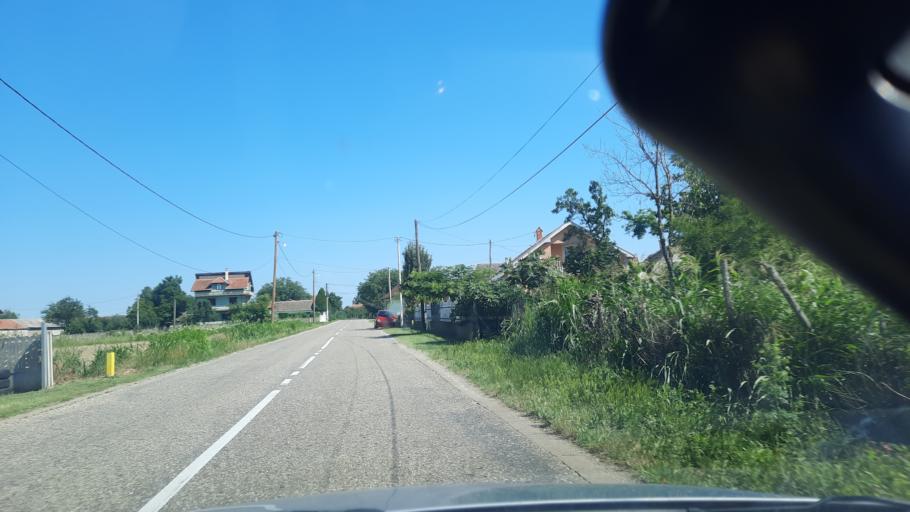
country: RS
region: Central Serbia
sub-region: Branicevski Okrug
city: Malo Crnice
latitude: 44.5917
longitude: 21.2725
